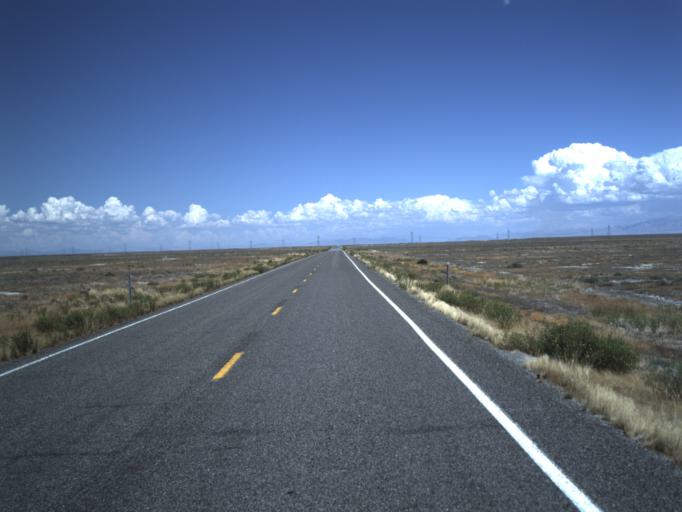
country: US
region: Utah
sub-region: Millard County
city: Delta
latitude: 39.2261
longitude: -112.9391
